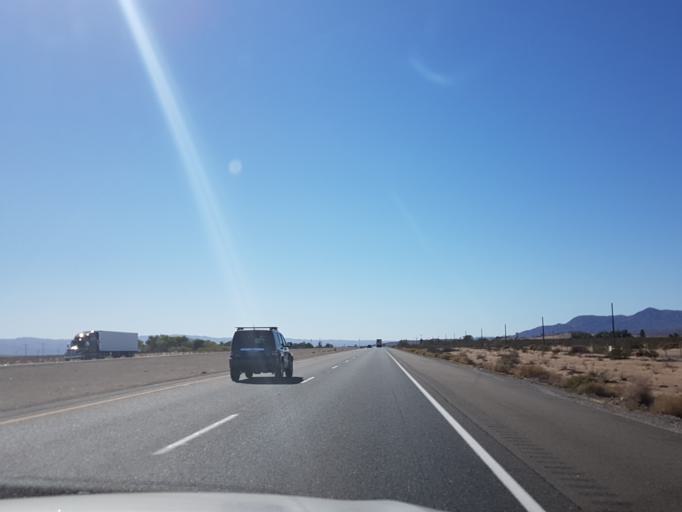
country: US
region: California
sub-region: San Bernardino County
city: Fort Irwin
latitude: 34.9561
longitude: -116.6626
